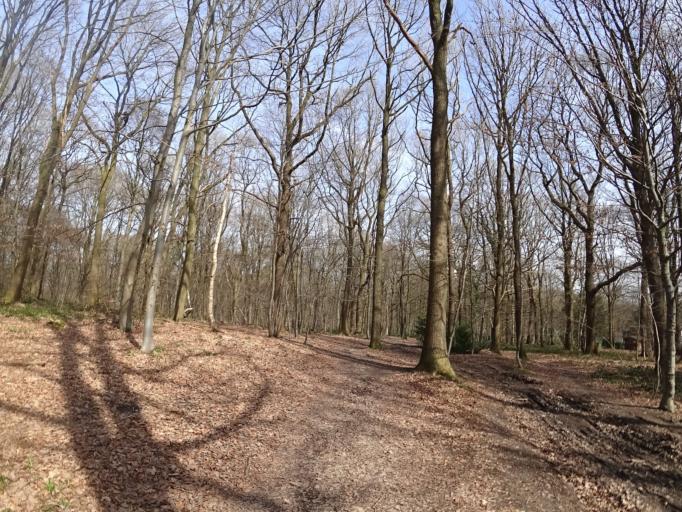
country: BE
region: Wallonia
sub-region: Province de Namur
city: Namur
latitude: 50.4423
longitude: 4.8363
